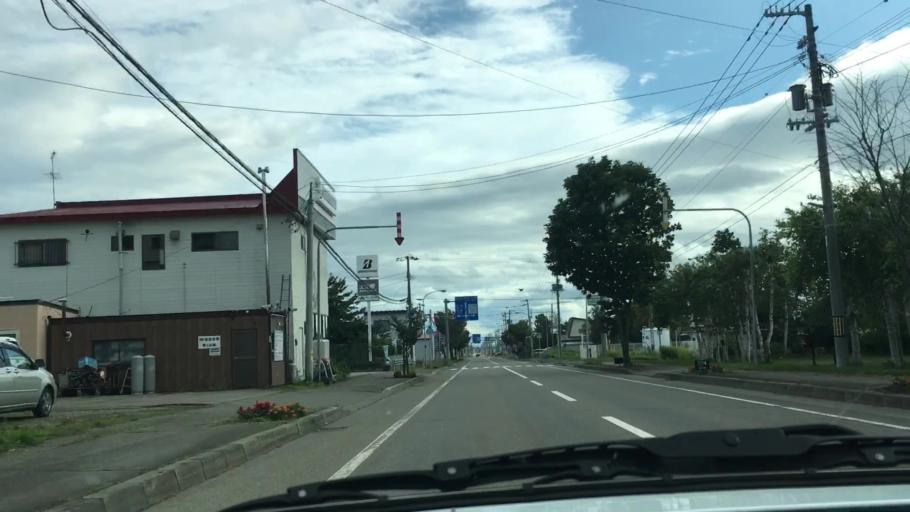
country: JP
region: Hokkaido
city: Otofuke
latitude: 43.2377
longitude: 143.2962
